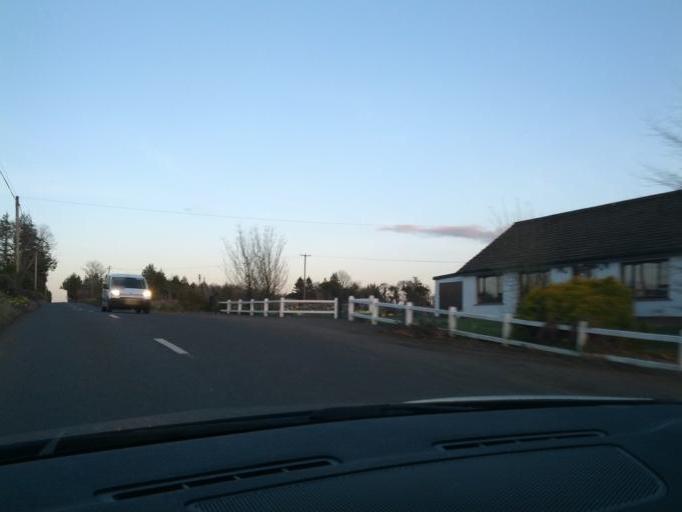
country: IE
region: Connaught
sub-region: Roscommon
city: Boyle
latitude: 53.9699
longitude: -8.3827
